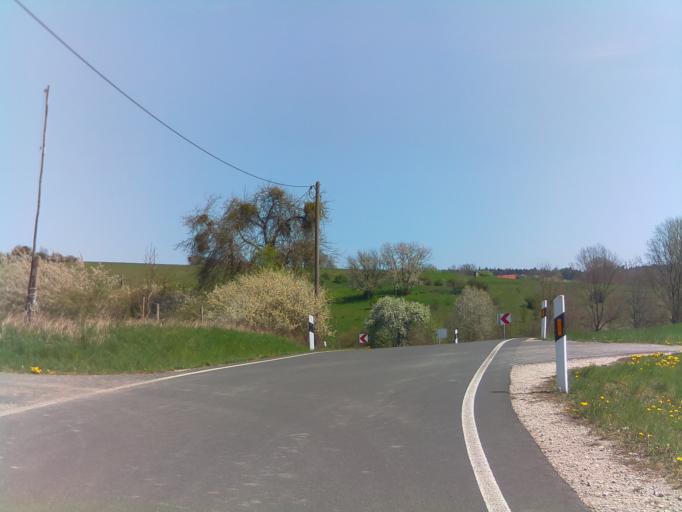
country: DE
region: Thuringia
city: Hildburghausen
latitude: 50.3761
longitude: 10.7508
